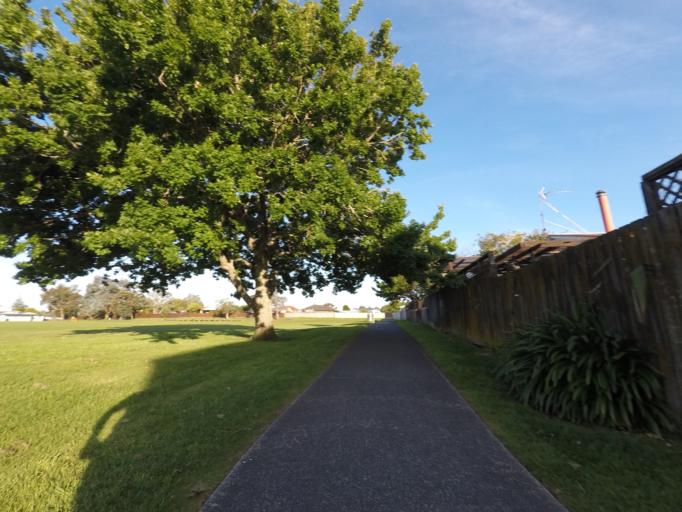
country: NZ
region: Auckland
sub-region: Auckland
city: Rosebank
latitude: -36.8397
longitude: 174.6433
